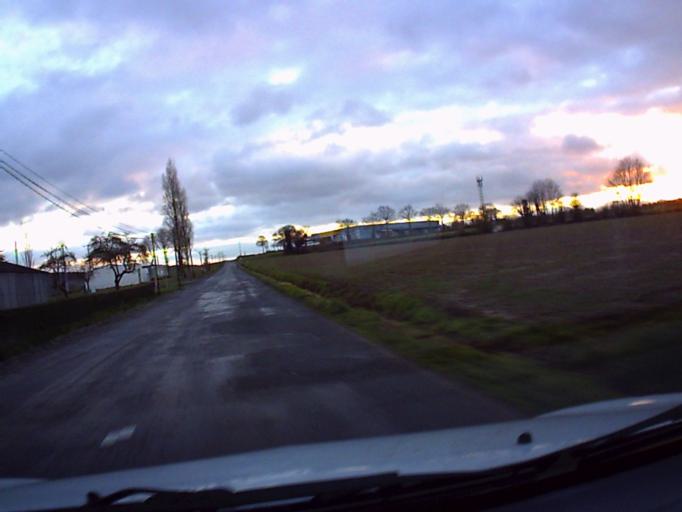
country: FR
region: Brittany
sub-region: Departement d'Ille-et-Vilaine
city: Iffendic
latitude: 48.1226
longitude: -2.0411
